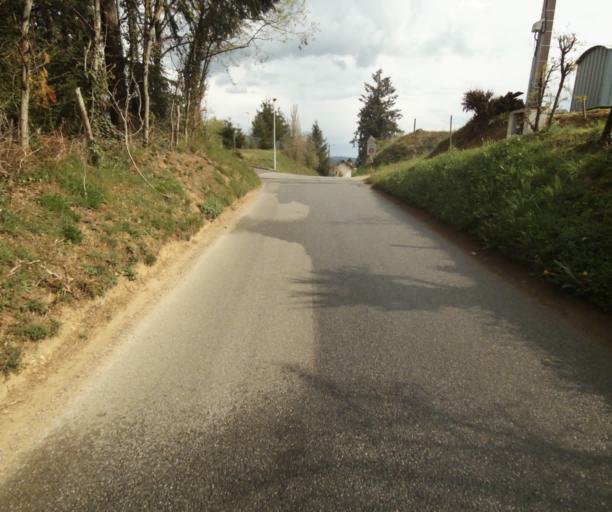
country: FR
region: Limousin
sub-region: Departement de la Correze
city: Tulle
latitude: 45.2758
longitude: 1.7515
